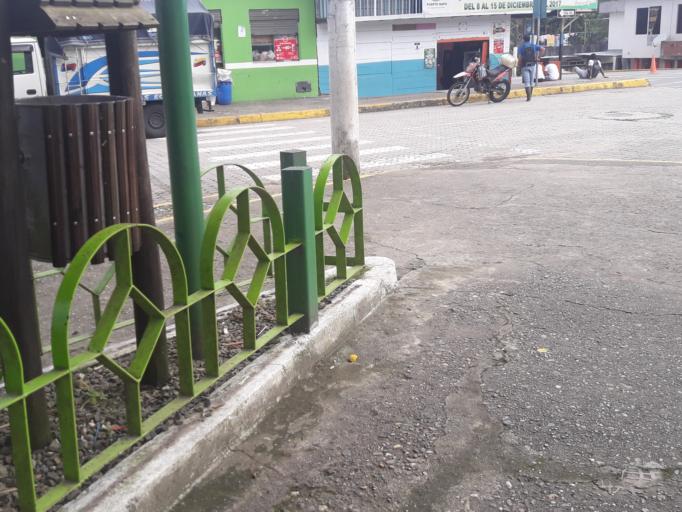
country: EC
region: Napo
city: Tena
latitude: -1.0428
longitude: -77.7950
